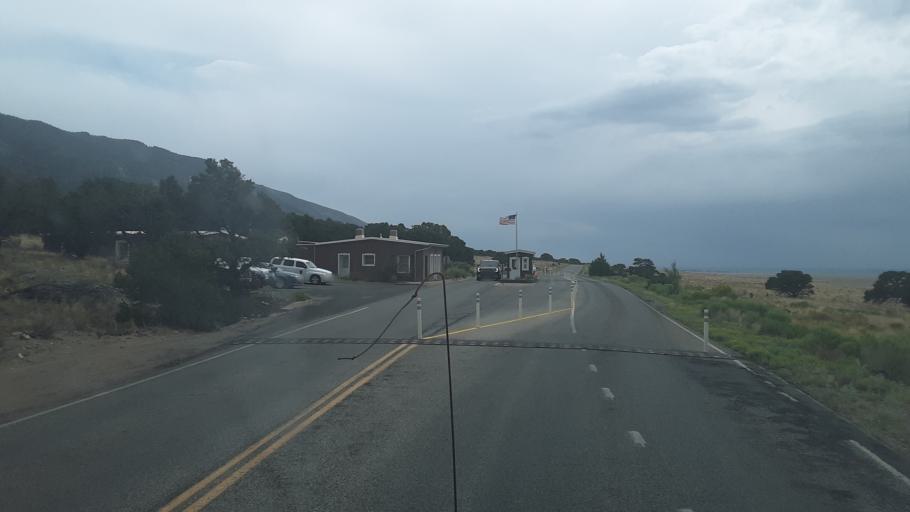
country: US
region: Colorado
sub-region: Alamosa County
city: Alamosa East
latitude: 37.7257
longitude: -105.5188
